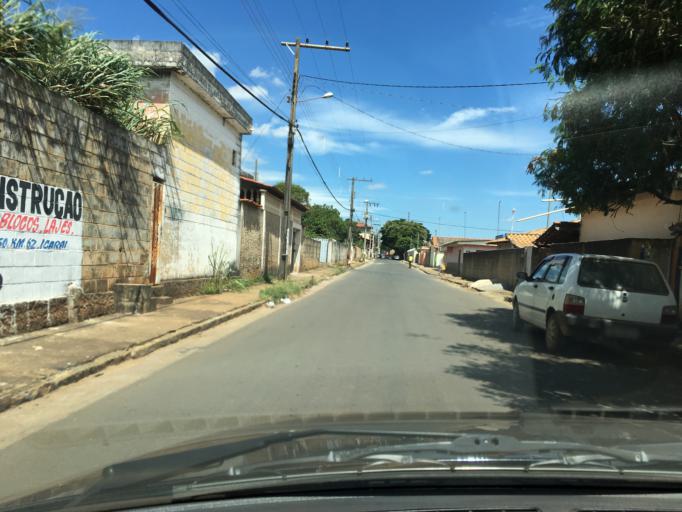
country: BR
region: Minas Gerais
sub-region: Mateus Leme
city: Mateus Leme
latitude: -19.9935
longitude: -44.4299
